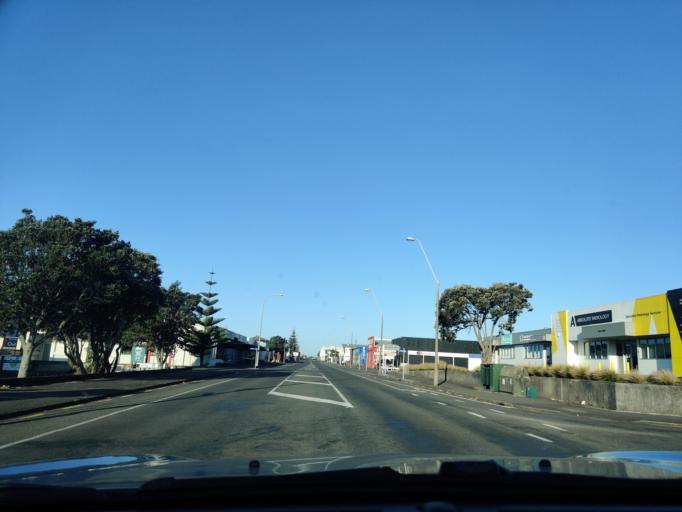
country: NZ
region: Taranaki
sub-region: New Plymouth District
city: New Plymouth
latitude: -39.0546
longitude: 174.0780
